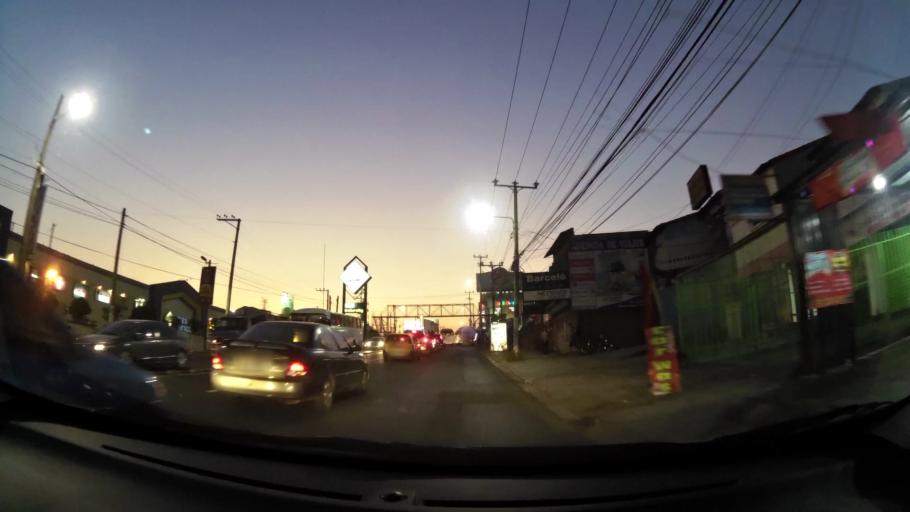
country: SV
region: La Libertad
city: Antiguo Cuscatlan
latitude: 13.6811
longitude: -89.2478
